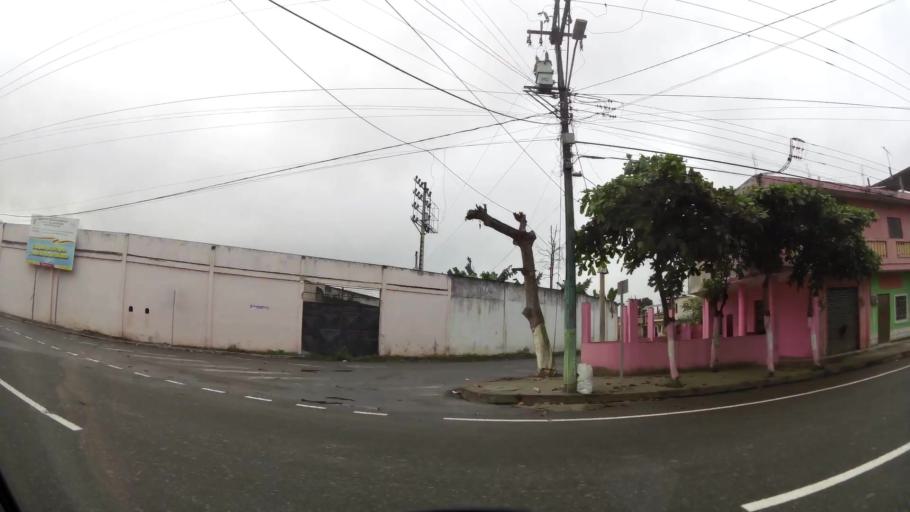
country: EC
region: El Oro
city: Pasaje
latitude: -3.3292
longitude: -79.8155
